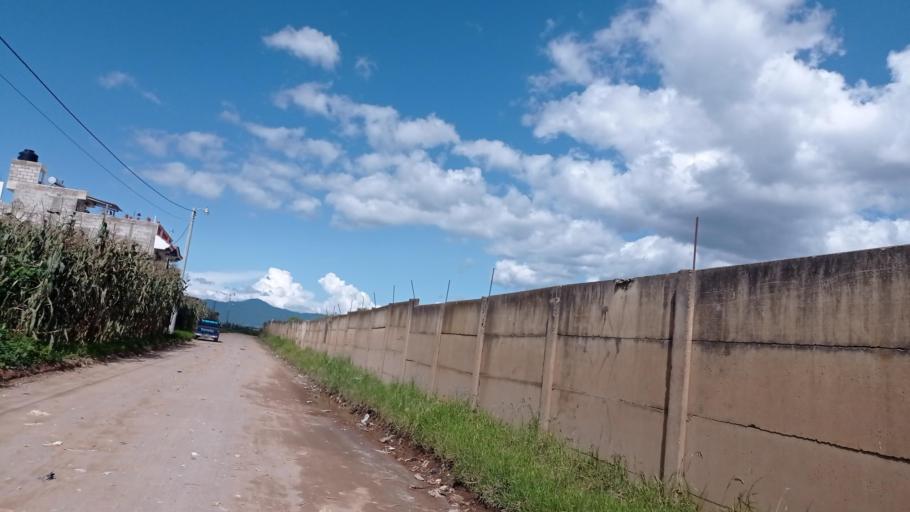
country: GT
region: Quetzaltenango
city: Olintepeque
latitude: 14.8715
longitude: -91.4963
